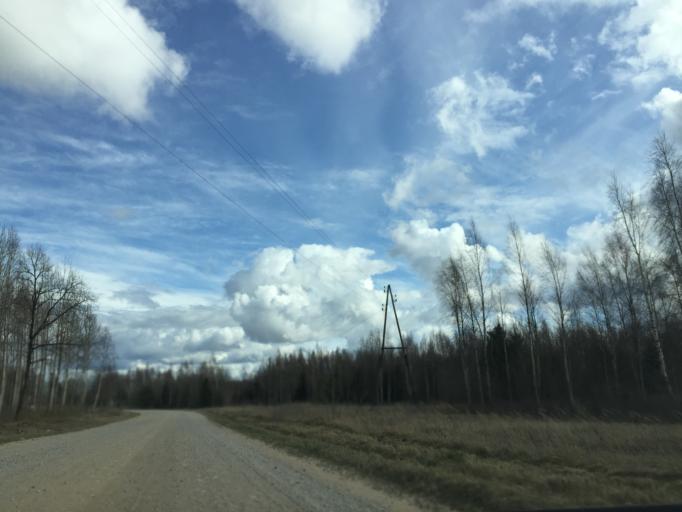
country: LV
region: Limbazu Rajons
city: Limbazi
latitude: 57.6037
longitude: 24.8001
